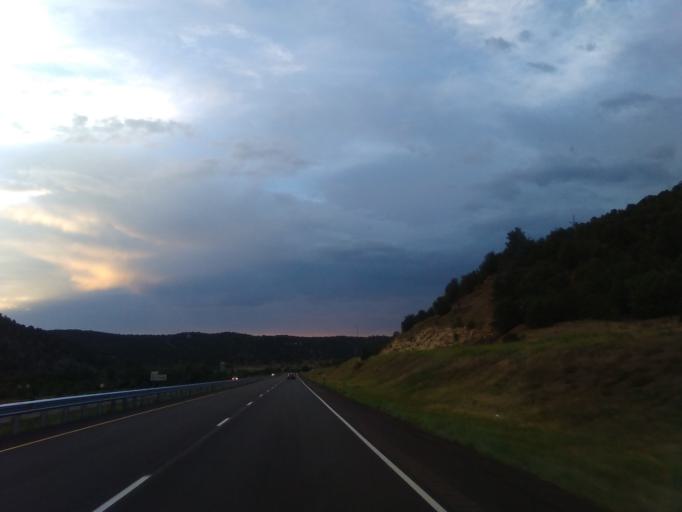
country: US
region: Colorado
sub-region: Las Animas County
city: Trinidad
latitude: 37.0978
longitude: -104.5203
